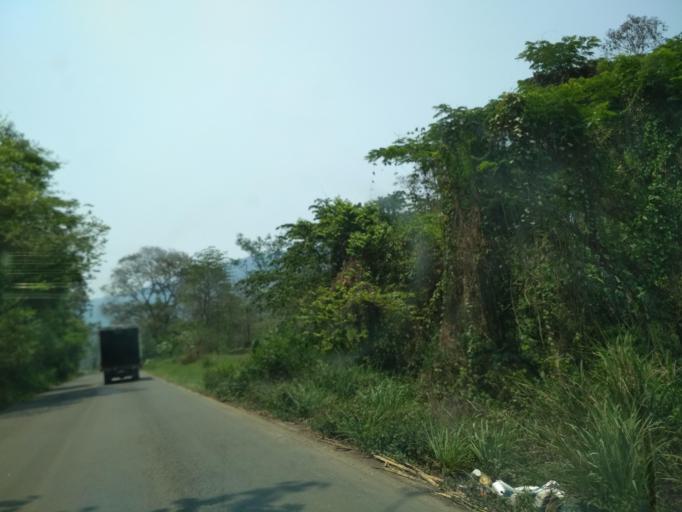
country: MX
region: Veracruz
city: Tezonapa
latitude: 18.6068
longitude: -96.6915
